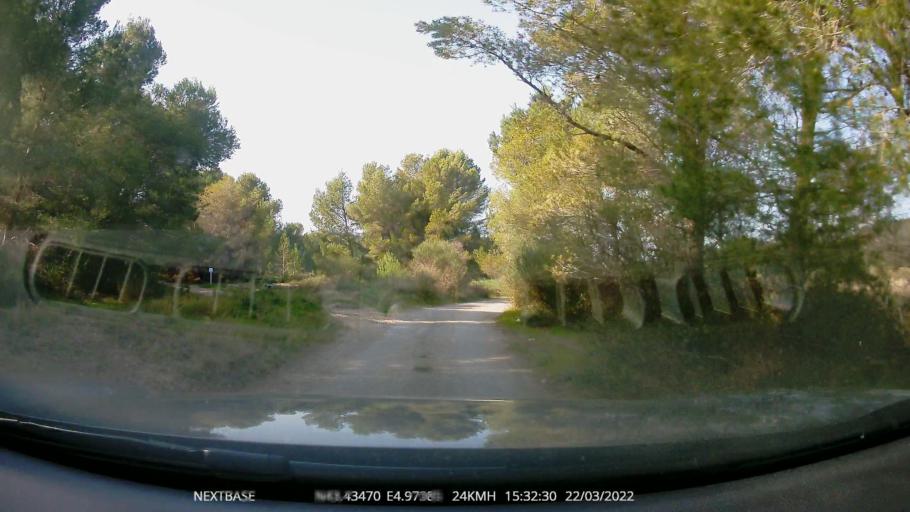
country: FR
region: Provence-Alpes-Cote d'Azur
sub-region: Departement des Bouches-du-Rhone
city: Port-de-Bouc
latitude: 43.4347
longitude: 4.9738
